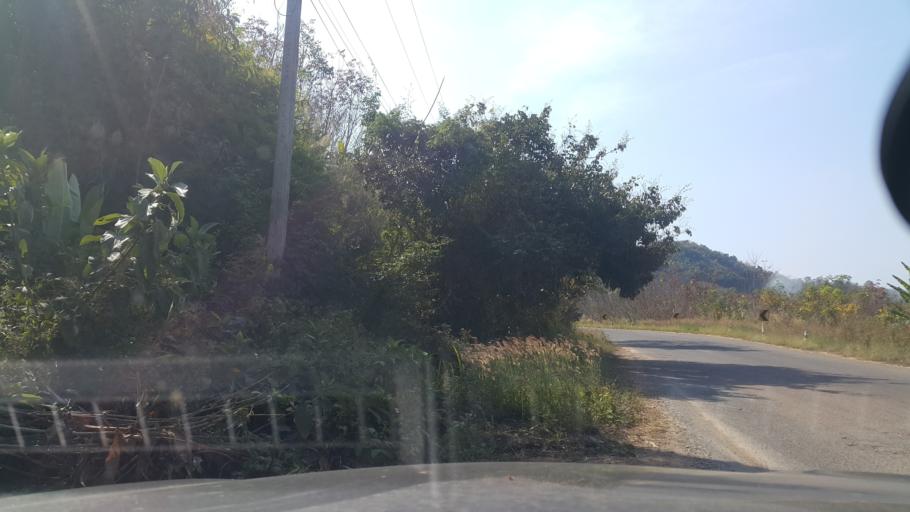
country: TH
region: Loei
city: Pak Chom
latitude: 18.1107
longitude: 102.0014
